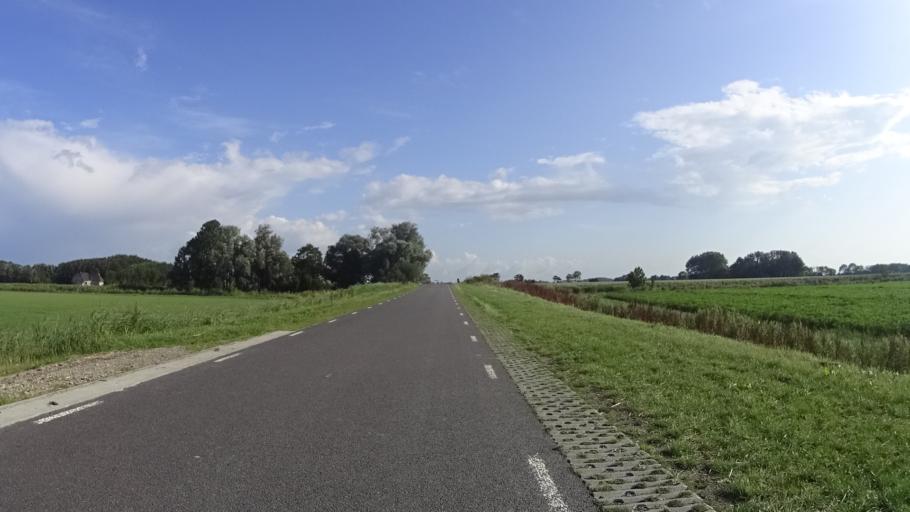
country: NL
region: Friesland
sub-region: Gemeente Harlingen
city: Harlingen
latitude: 53.1321
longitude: 5.4591
